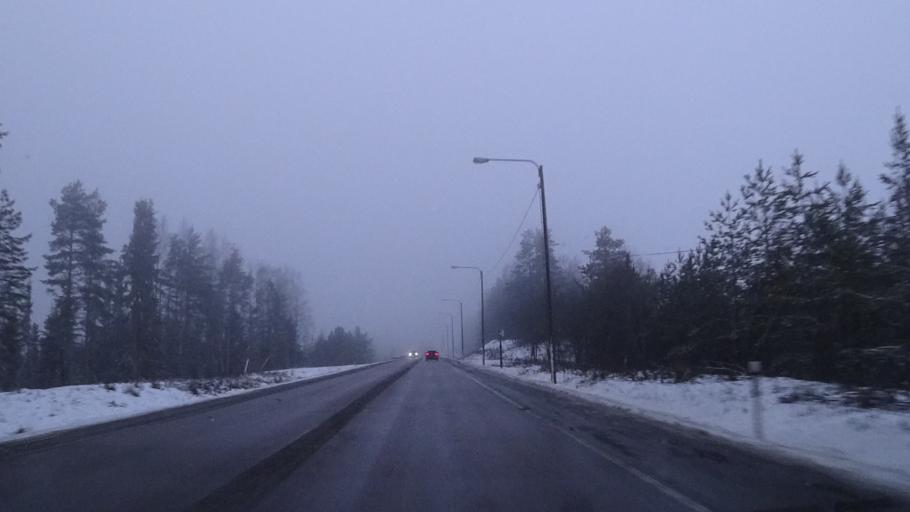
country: FI
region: Paijanne Tavastia
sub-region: Lahti
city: Hollola
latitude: 60.9865
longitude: 25.4020
